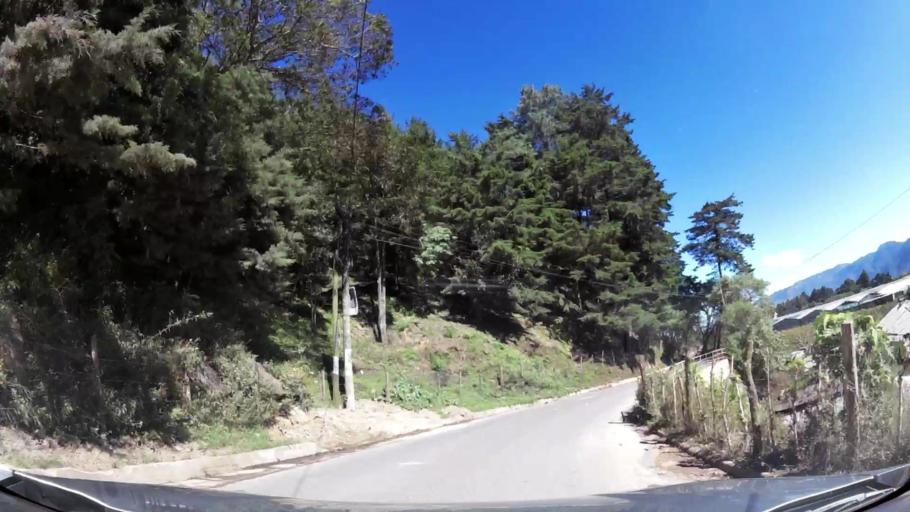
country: GT
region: Guatemala
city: San Jose Pinula
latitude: 14.5357
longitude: -90.4161
